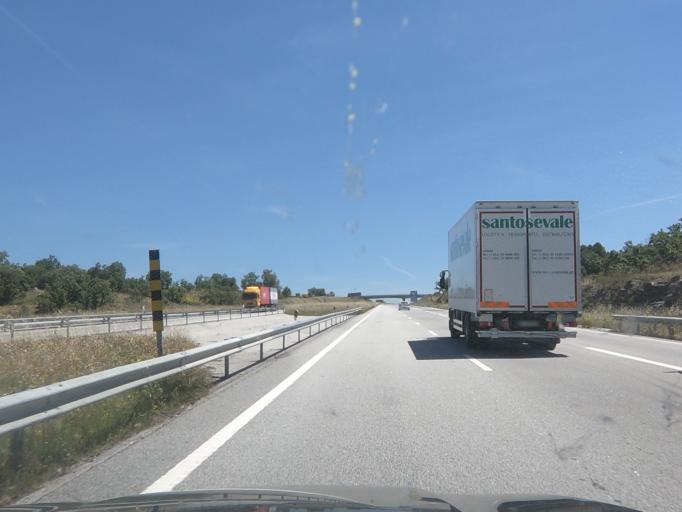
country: PT
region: Guarda
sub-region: Pinhel
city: Pinhel
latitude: 40.6076
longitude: -7.0135
